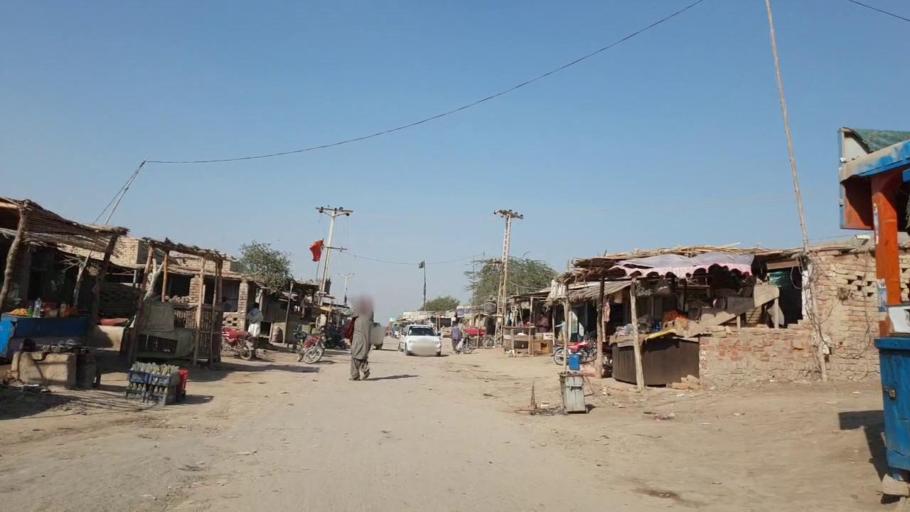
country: PK
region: Sindh
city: Digri
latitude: 25.0322
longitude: 69.1051
